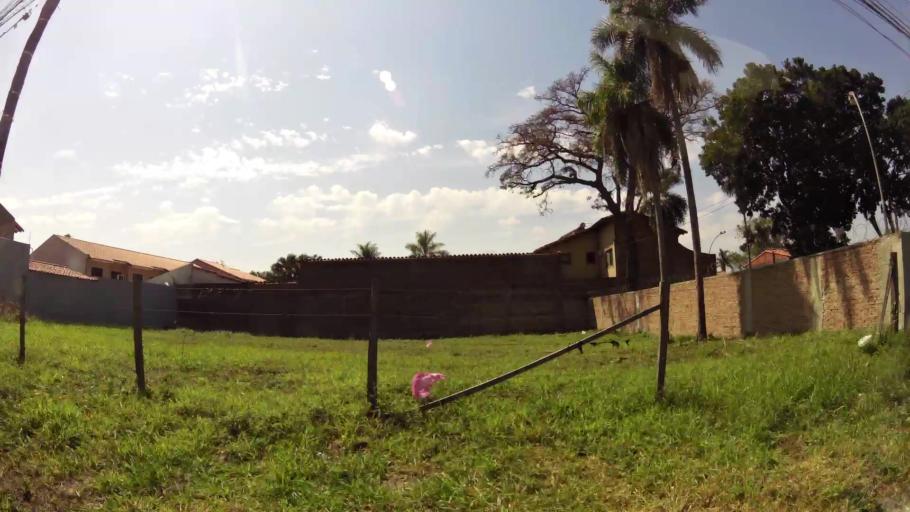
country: BO
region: Santa Cruz
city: Santa Cruz de la Sierra
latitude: -17.7436
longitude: -63.1576
